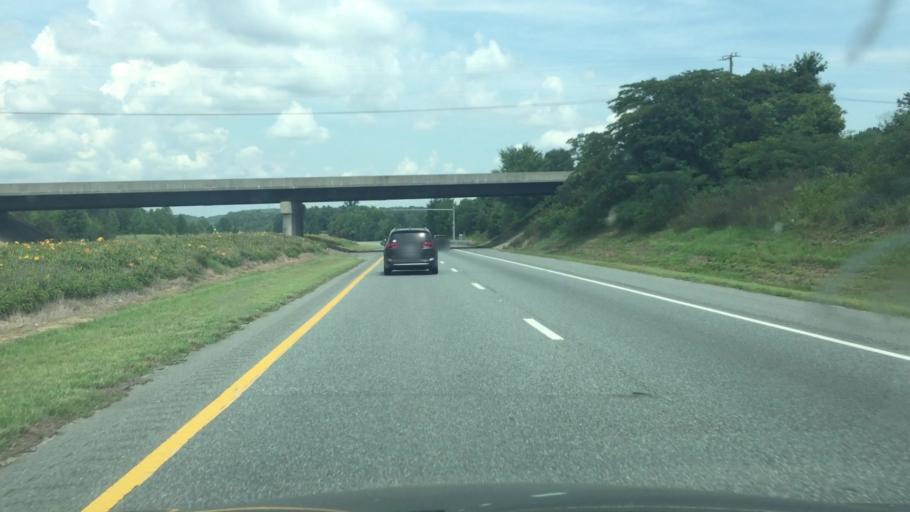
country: US
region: North Carolina
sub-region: Montgomery County
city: Biscoe
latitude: 35.4885
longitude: -79.7803
